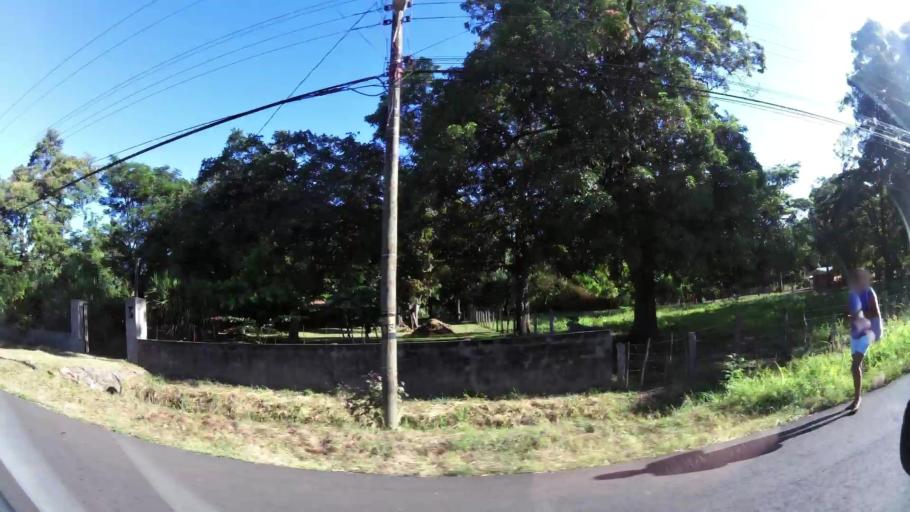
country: CR
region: Guanacaste
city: Sardinal
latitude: 10.4923
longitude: -85.6338
